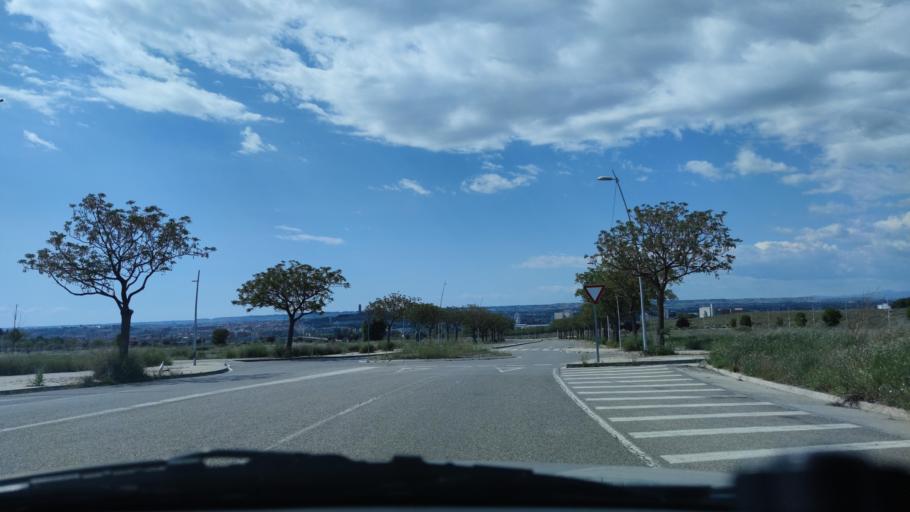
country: ES
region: Catalonia
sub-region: Provincia de Lleida
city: Lleida
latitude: 41.6028
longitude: 0.6637
